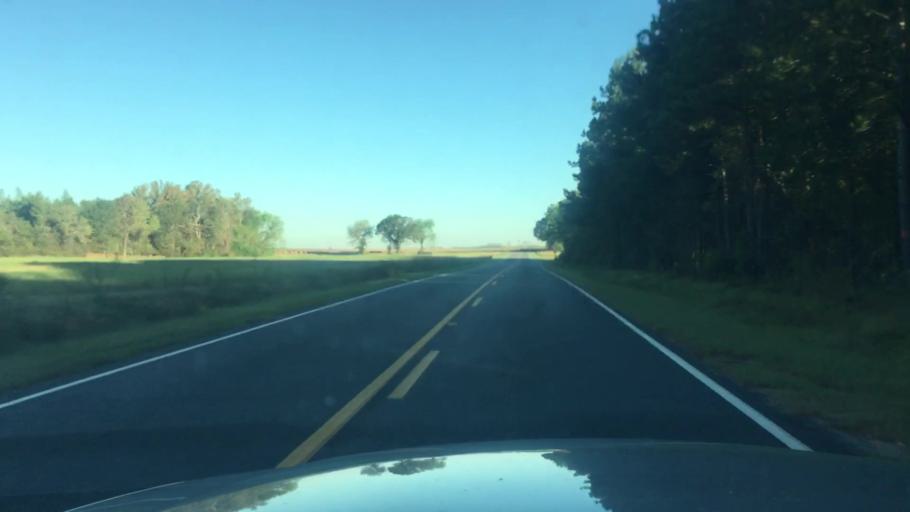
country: US
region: North Carolina
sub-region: Harnett County
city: Walkertown
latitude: 35.2810
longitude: -78.8669
